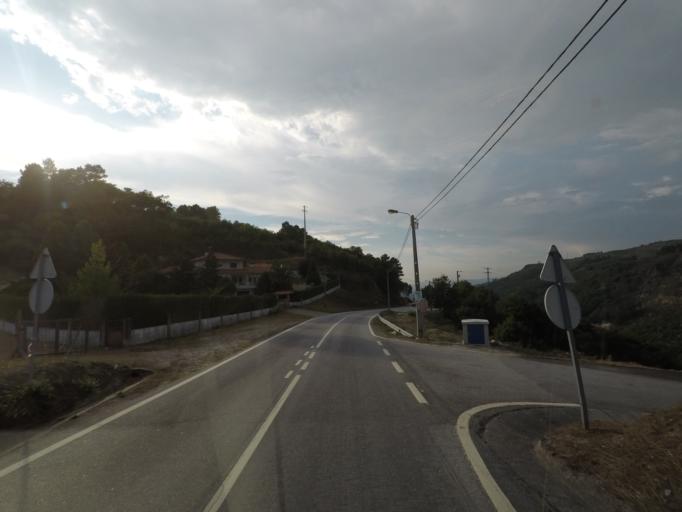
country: PT
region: Porto
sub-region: Baiao
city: Valadares
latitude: 41.2155
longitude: -7.9809
